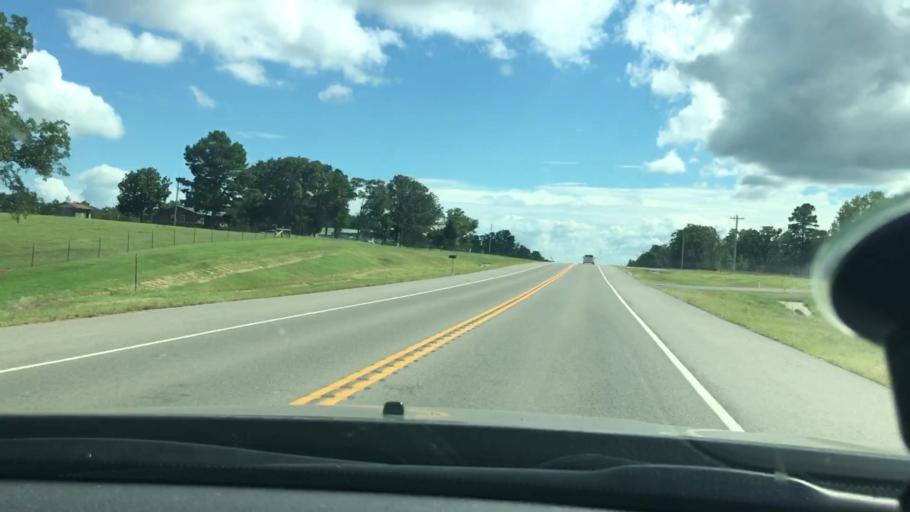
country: US
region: Oklahoma
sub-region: Sequoyah County
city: Vian
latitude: 35.6024
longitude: -94.9763
